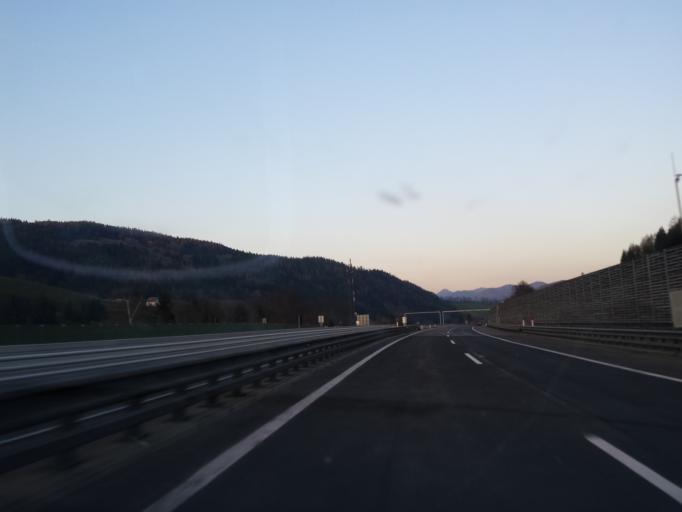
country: AT
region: Styria
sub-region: Politischer Bezirk Bruck-Muerzzuschlag
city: Muerzzuschlag
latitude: 47.6023
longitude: 15.6921
